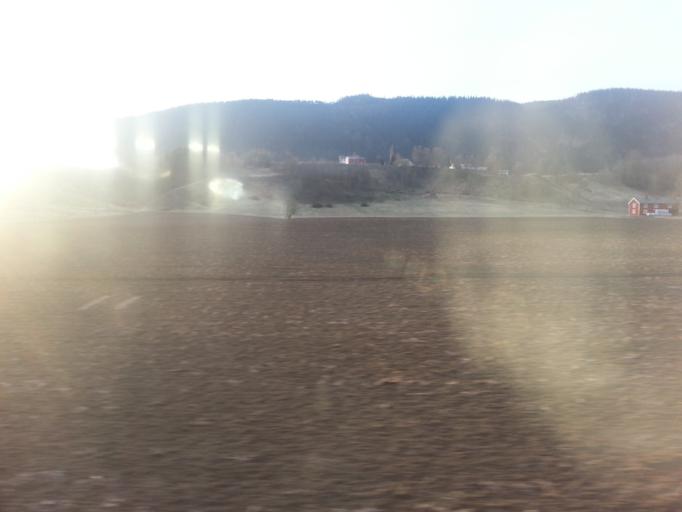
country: NO
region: Sor-Trondelag
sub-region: Melhus
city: Lundamo
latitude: 63.1701
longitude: 10.3013
